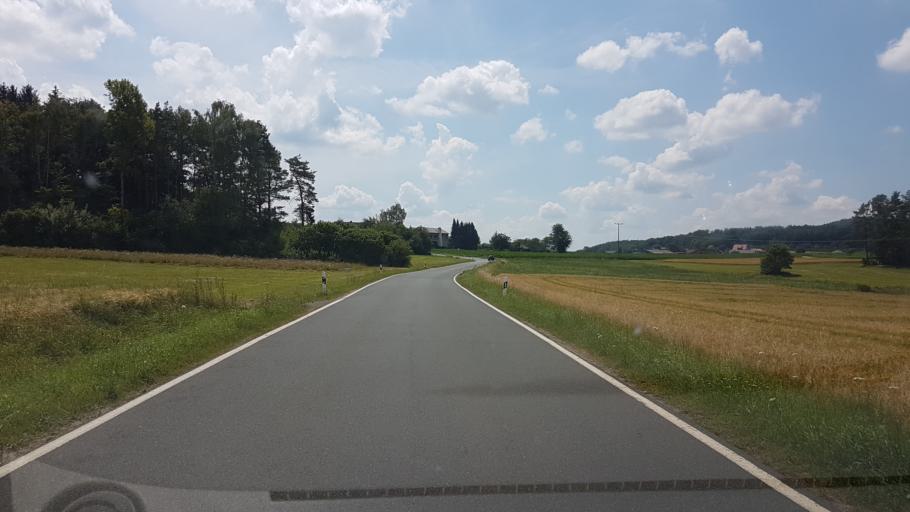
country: DE
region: Bavaria
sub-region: Upper Franconia
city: Egloffstein
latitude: 49.7606
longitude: 11.2659
